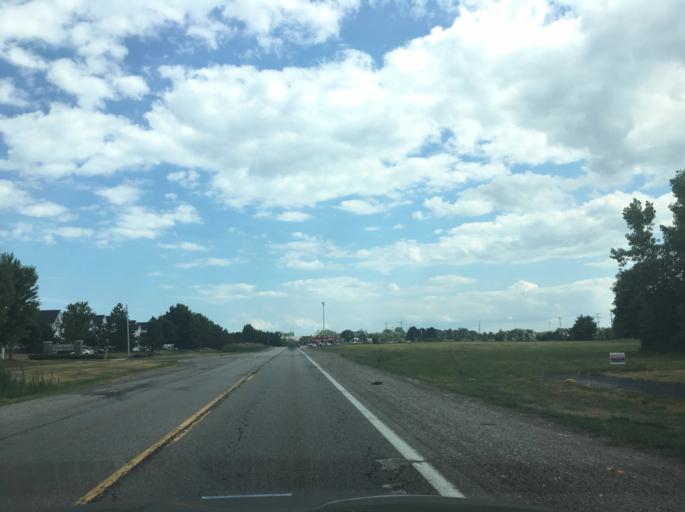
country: US
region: Michigan
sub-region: Macomb County
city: Clinton
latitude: 42.6316
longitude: -82.9553
